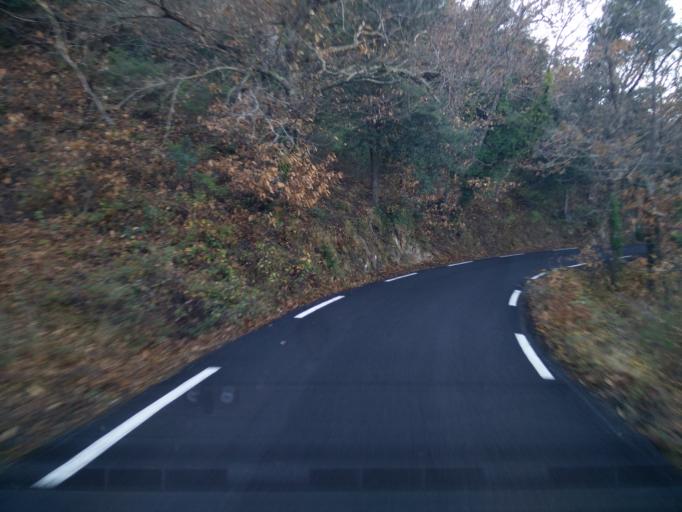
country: FR
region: Provence-Alpes-Cote d'Azur
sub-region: Departement du Var
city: Collobrieres
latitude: 43.2398
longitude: 6.3449
